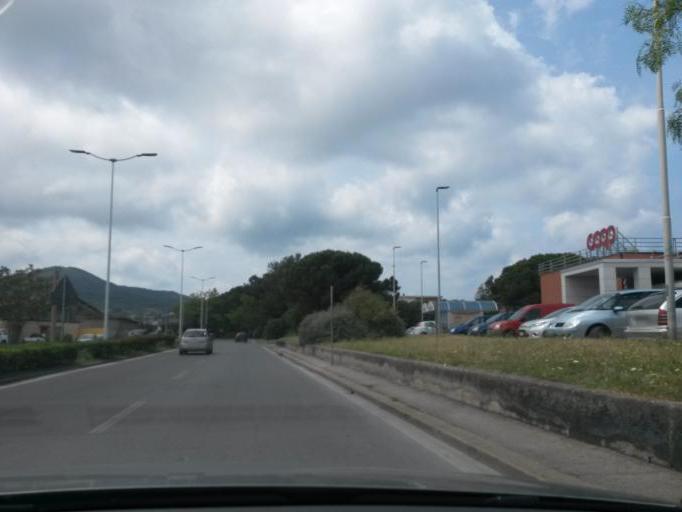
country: IT
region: Tuscany
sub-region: Provincia di Livorno
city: Portoferraio
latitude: 42.8110
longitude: 10.3189
